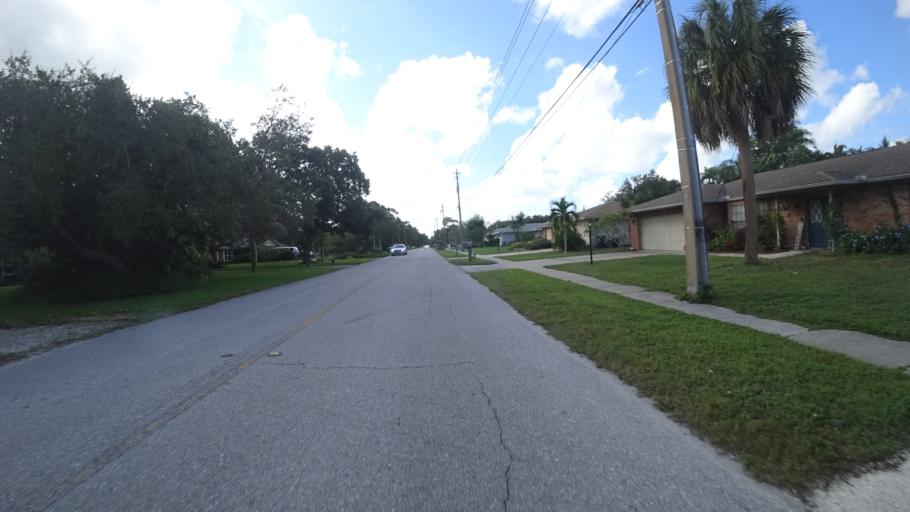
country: US
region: Florida
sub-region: Manatee County
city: West Bradenton
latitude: 27.5117
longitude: -82.6324
